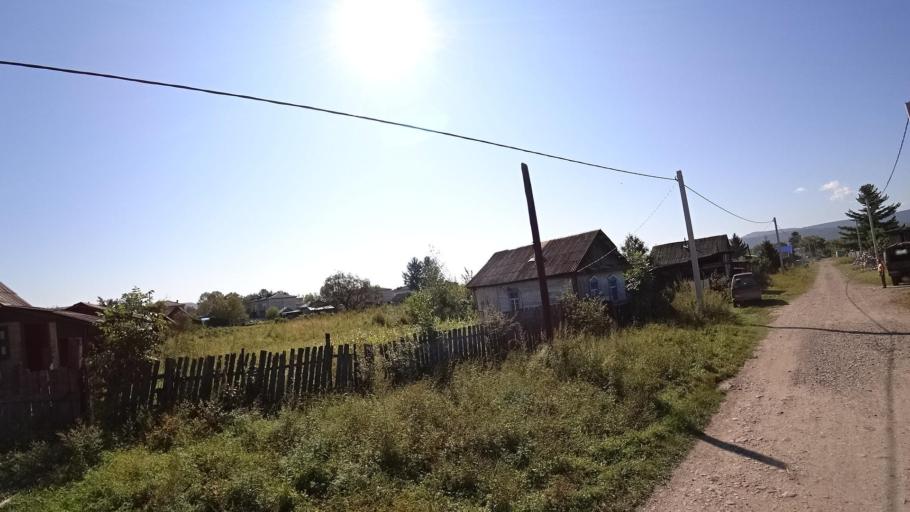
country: RU
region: Jewish Autonomous Oblast
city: Bira
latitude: 48.9989
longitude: 132.4504
